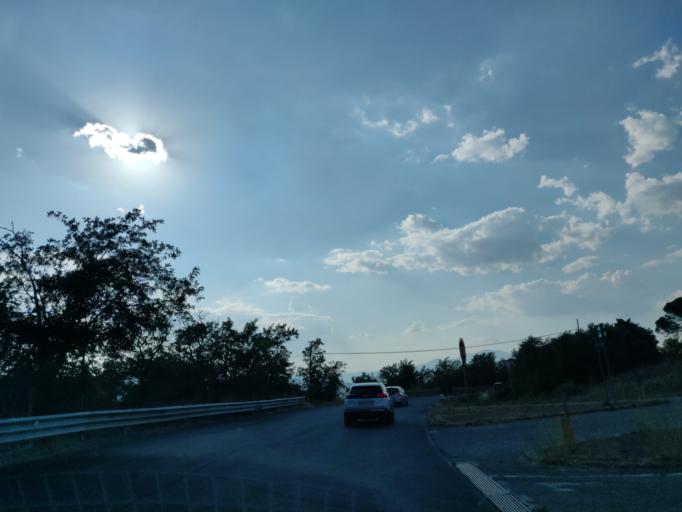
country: IT
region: Latium
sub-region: Provincia di Viterbo
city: Proceno
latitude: 42.7716
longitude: 11.8524
